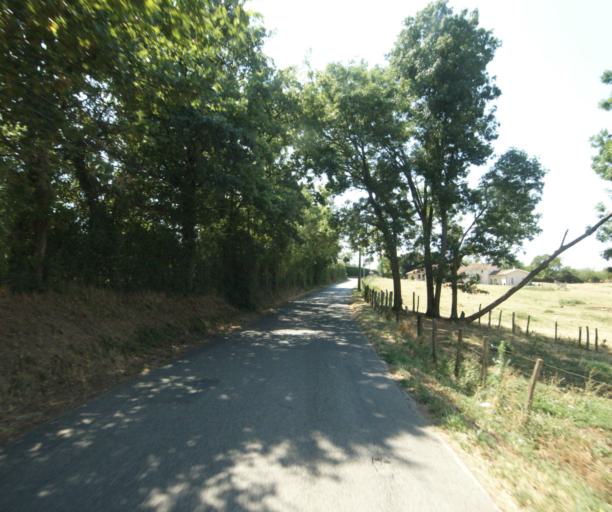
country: FR
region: Rhone-Alpes
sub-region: Departement du Rhone
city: Sourcieux-les-Mines
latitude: 45.8089
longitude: 4.6226
